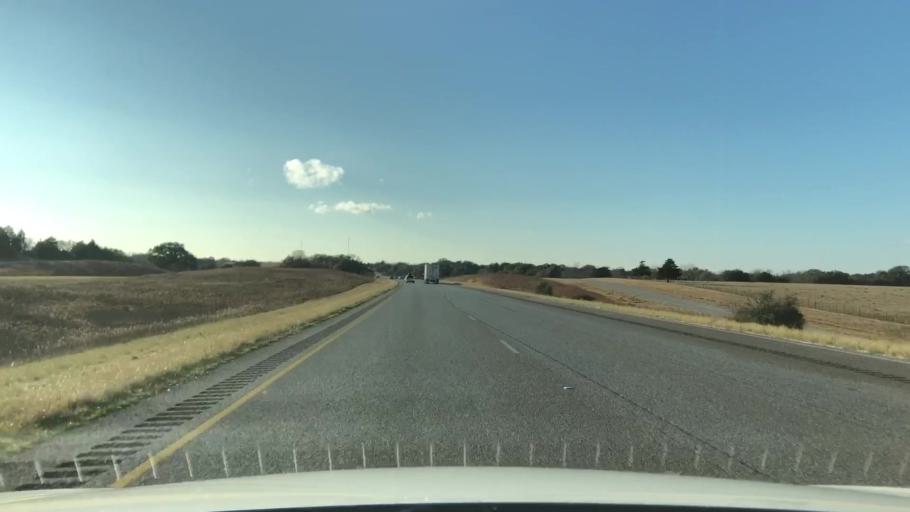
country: US
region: Texas
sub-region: Fayette County
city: Flatonia
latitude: 29.6973
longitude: -97.0402
